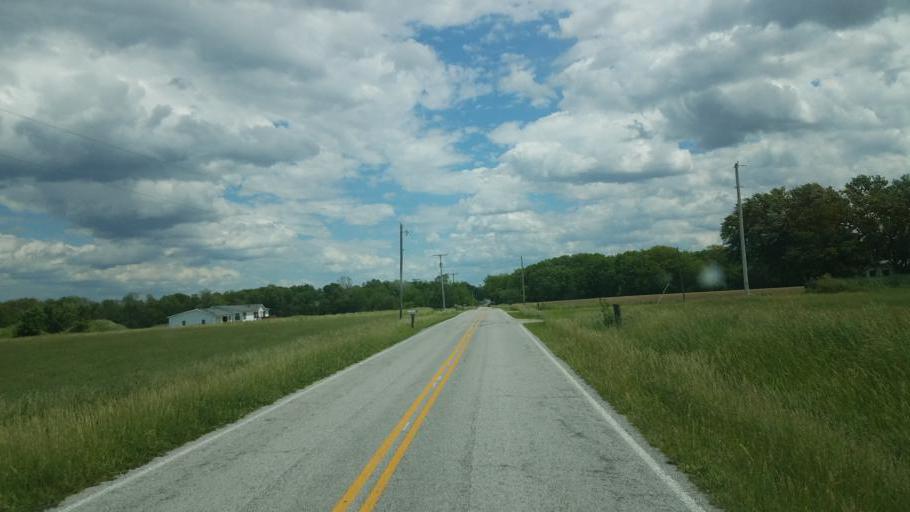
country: US
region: Ohio
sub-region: Huron County
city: Monroeville
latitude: 41.1850
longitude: -82.7326
